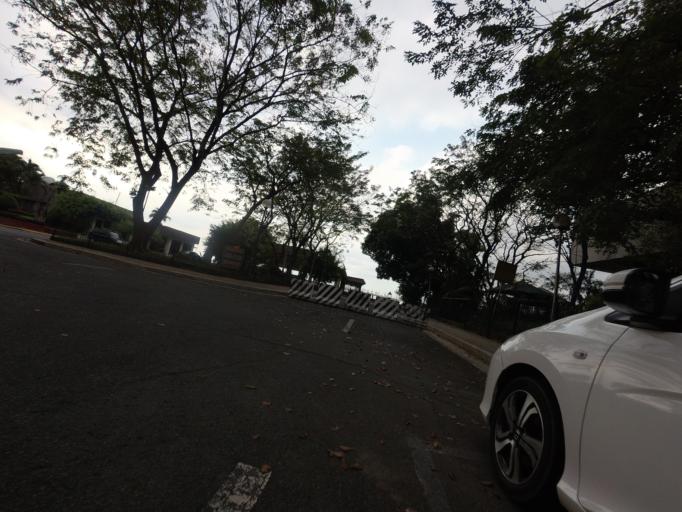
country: PH
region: Metro Manila
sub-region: City of Manila
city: Port Area
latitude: 14.5565
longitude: 120.9803
